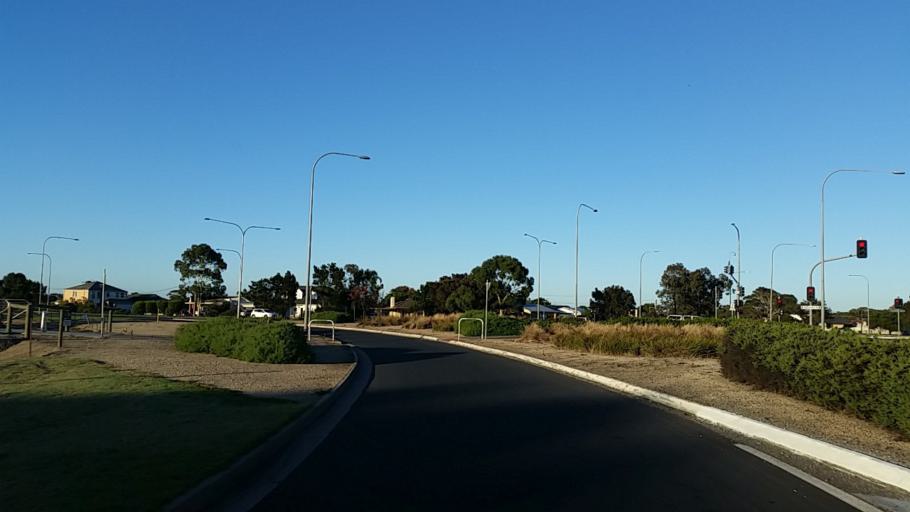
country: AU
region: South Australia
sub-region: Charles Sturt
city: Henley Beach
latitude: -34.9344
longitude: 138.5181
